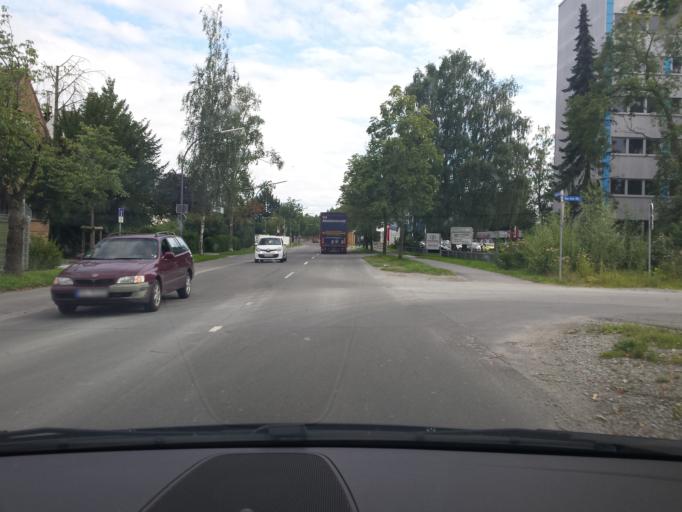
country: DE
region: North Rhine-Westphalia
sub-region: Regierungsbezirk Arnsberg
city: Lippstadt
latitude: 51.6896
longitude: 8.3421
